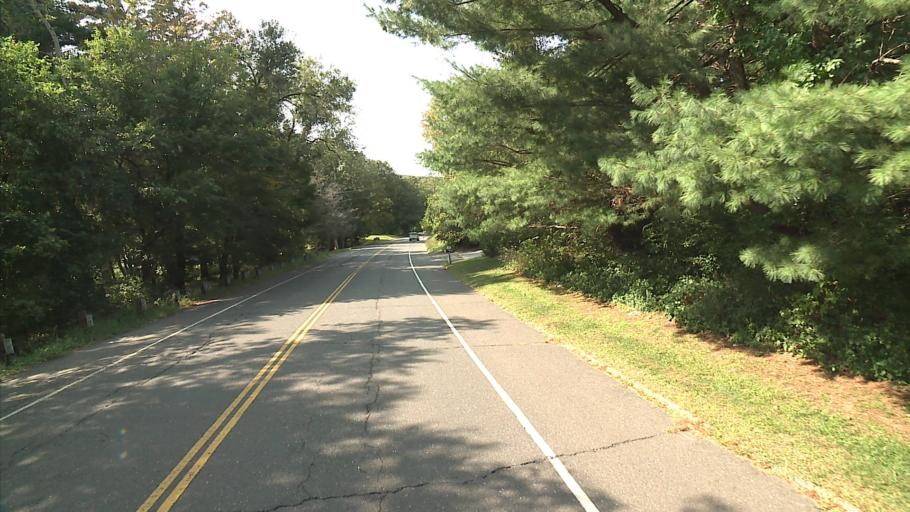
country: US
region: Connecticut
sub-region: New Haven County
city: Heritage Village
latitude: 41.4616
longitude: -73.2401
